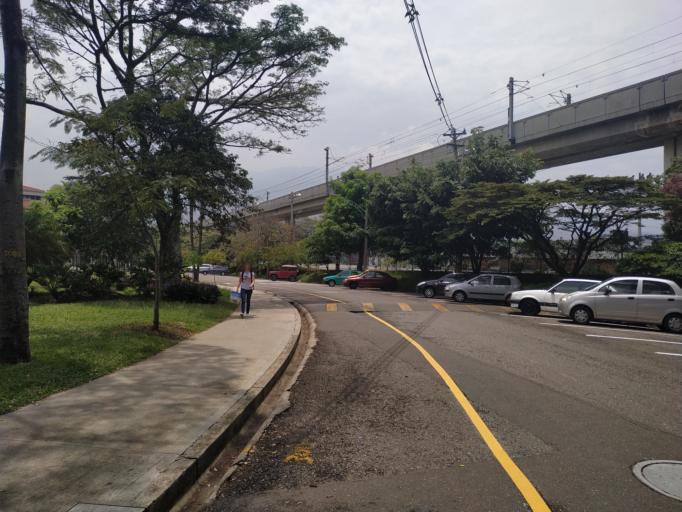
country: CO
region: Antioquia
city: Medellin
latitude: 6.2694
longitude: -75.5669
